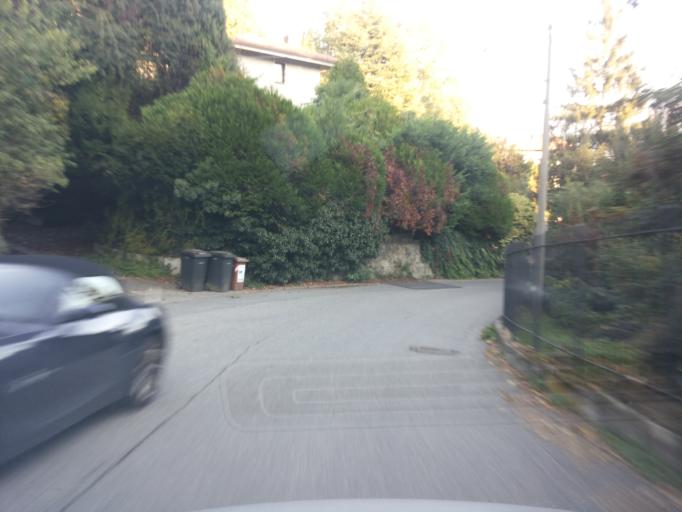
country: IT
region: Piedmont
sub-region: Provincia di Torino
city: Ivrea
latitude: 45.4543
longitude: 7.8725
